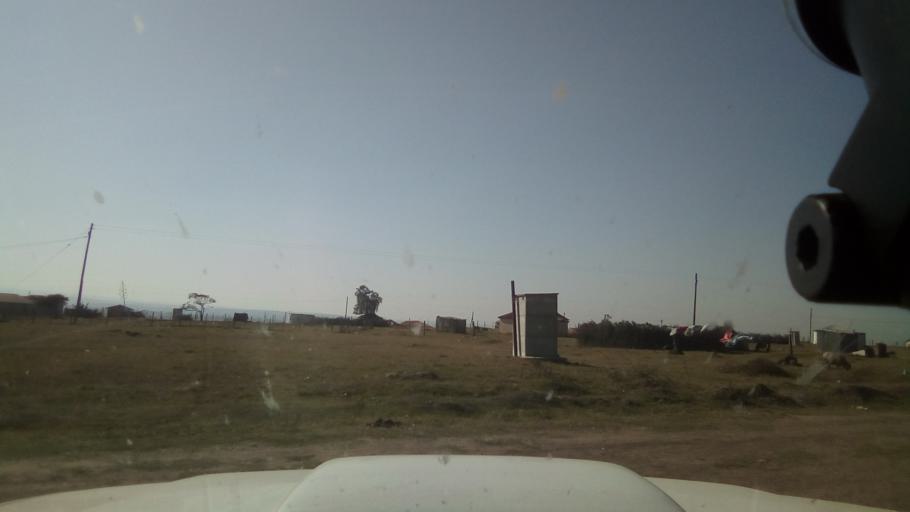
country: ZA
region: Eastern Cape
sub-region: Buffalo City Metropolitan Municipality
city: Bhisho
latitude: -32.9398
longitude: 27.3368
